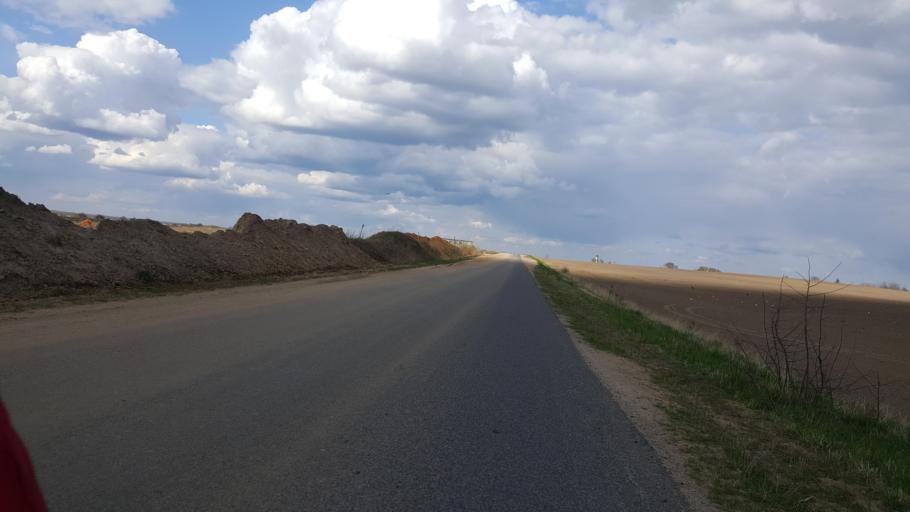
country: BY
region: Brest
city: Kamyanyets
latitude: 52.4366
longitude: 23.6506
